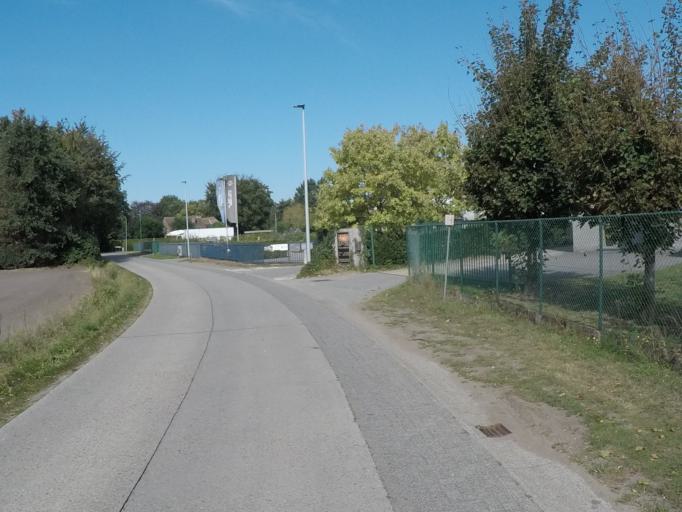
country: BE
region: Flanders
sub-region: Provincie Antwerpen
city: Lille
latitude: 51.2631
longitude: 4.8579
